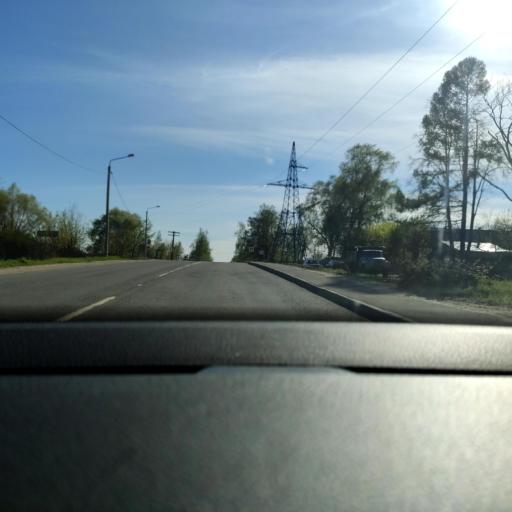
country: RU
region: Moskovskaya
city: Dmitrov
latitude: 56.3569
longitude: 37.5592
